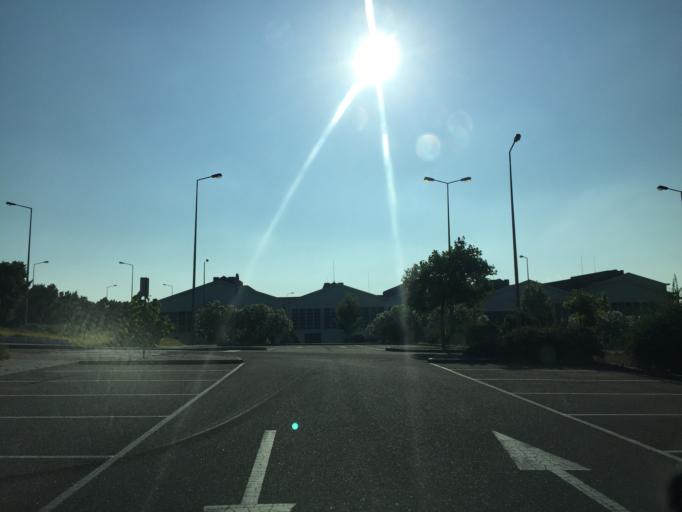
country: PT
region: Santarem
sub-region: Abrantes
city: Abrantes
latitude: 39.4754
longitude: -8.1888
